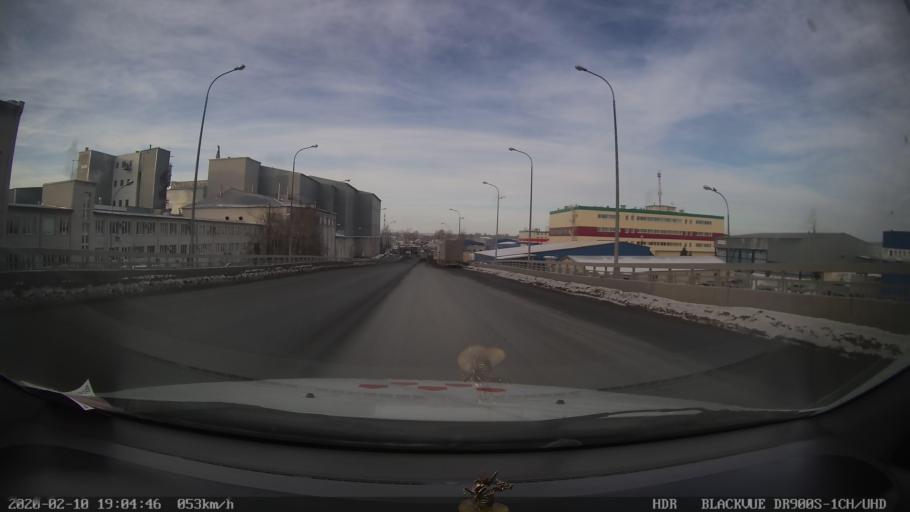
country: RU
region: Tatarstan
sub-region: Gorod Kazan'
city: Kazan
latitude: 55.7322
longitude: 49.1276
